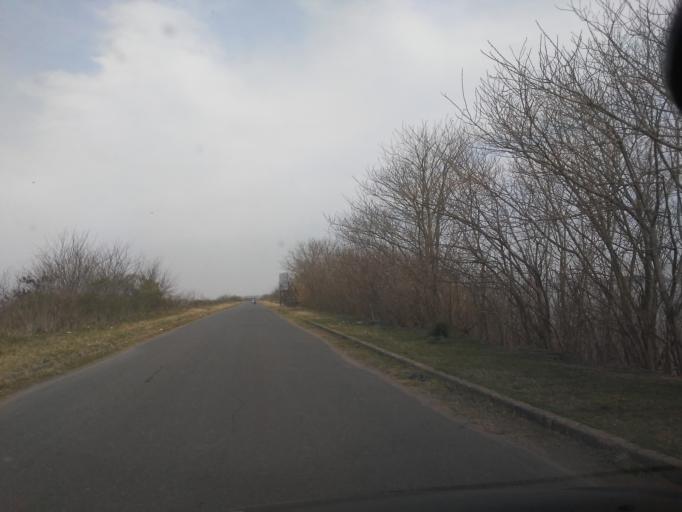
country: AR
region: Buenos Aires
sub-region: Partido de Marcos Paz
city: Marcos Paz
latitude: -34.6784
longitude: -58.8610
